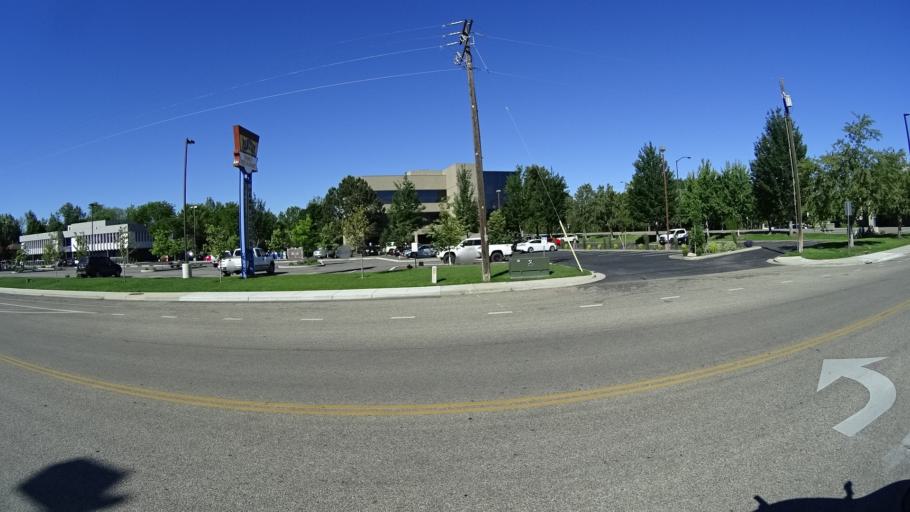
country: US
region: Idaho
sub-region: Ada County
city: Boise
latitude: 43.6162
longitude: -116.2195
